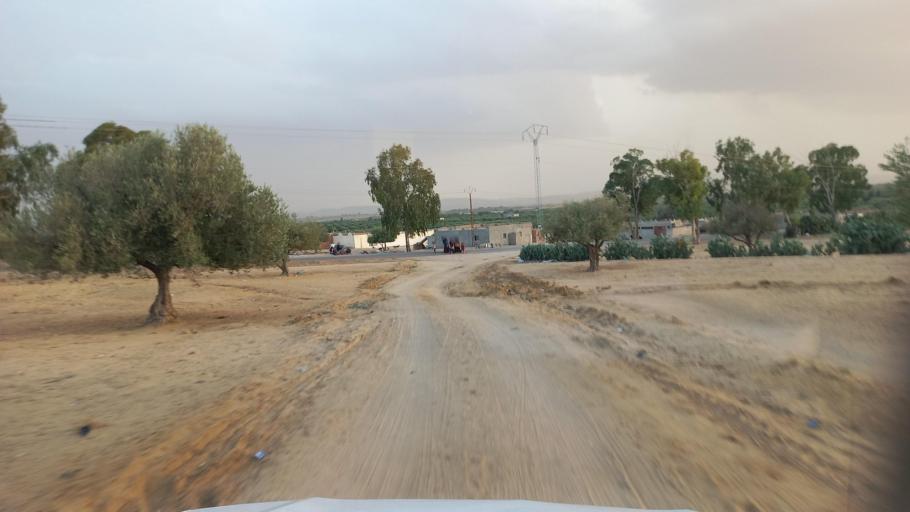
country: TN
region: Al Qasrayn
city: Kasserine
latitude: 35.2697
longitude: 9.0714
